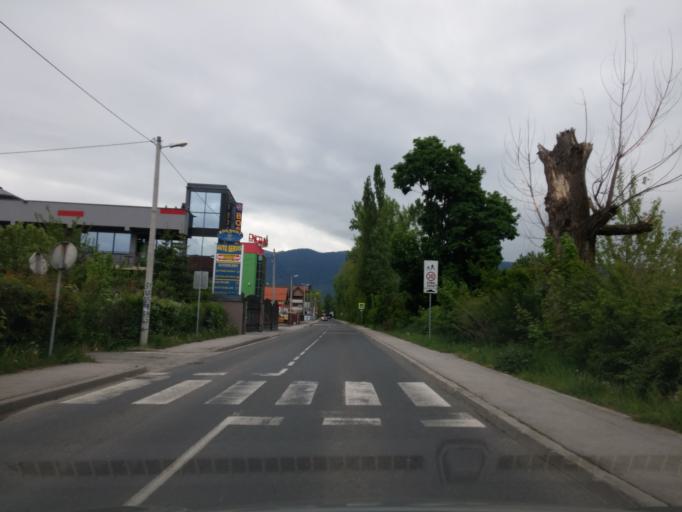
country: BA
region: Federation of Bosnia and Herzegovina
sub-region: Kanton Sarajevo
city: Sarajevo
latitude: 43.8374
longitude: 18.3336
